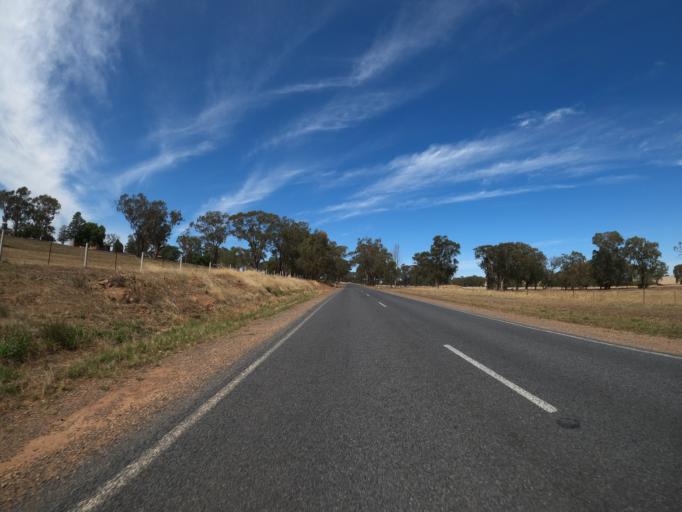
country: AU
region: Victoria
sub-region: Benalla
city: Benalla
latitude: -36.3319
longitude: 145.9608
